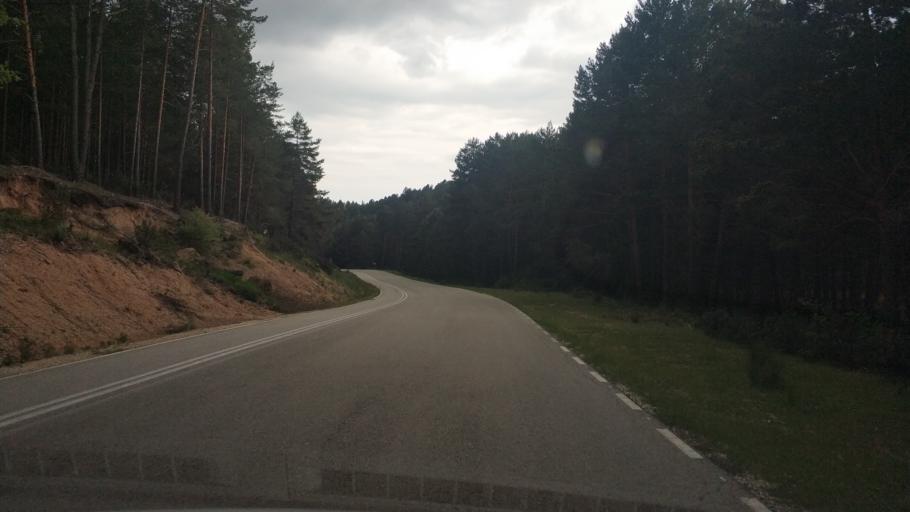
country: ES
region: Castille and Leon
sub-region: Provincia de Soria
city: San Leonardo de Yague
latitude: 41.8507
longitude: -3.0695
